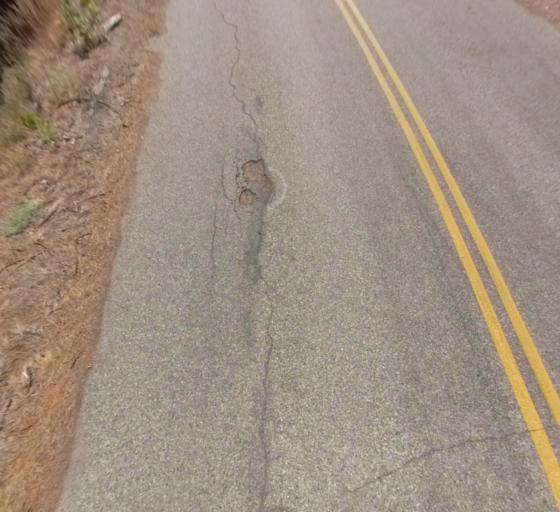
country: US
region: California
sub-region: Fresno County
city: Auberry
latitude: 37.3212
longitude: -119.3647
